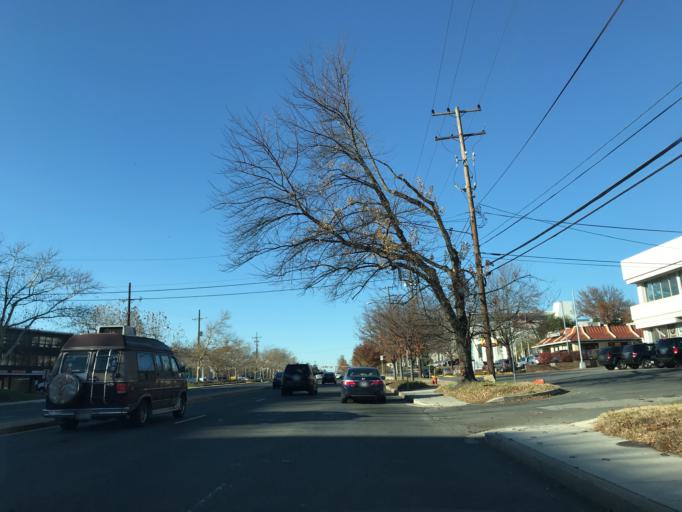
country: US
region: Maryland
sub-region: Montgomery County
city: North Bethesda
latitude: 39.0671
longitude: -77.1283
